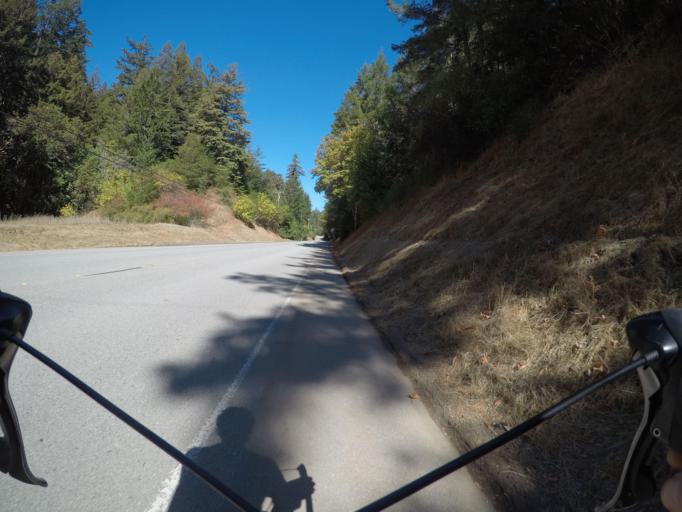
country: US
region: California
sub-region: San Mateo County
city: Portola Valley
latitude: 37.3019
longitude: -122.2666
